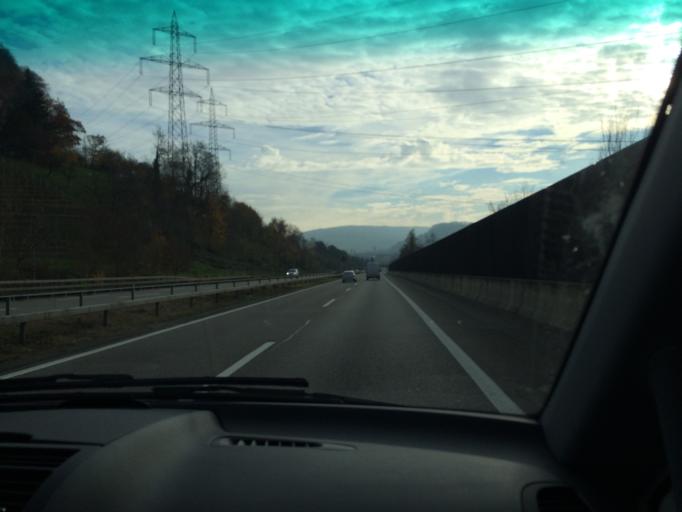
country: CH
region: Basel-Landschaft
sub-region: Bezirk Sissach
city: Itingen
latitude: 47.4740
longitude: 7.7841
